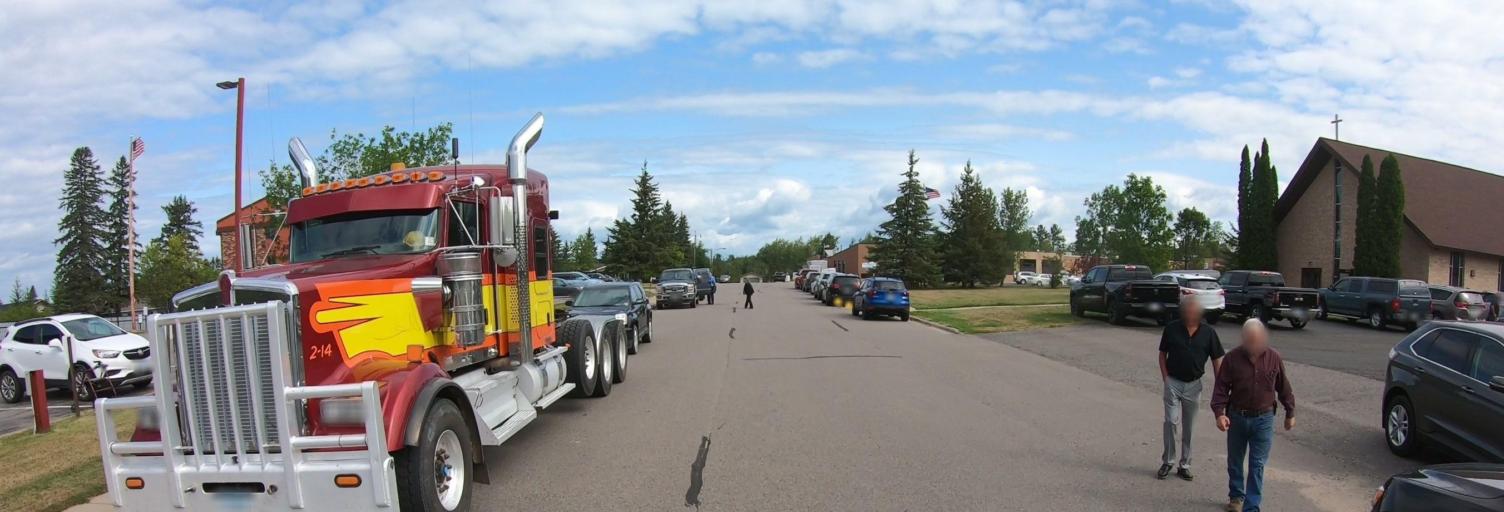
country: US
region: Minnesota
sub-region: Saint Louis County
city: Mountain Iron
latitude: 47.8517
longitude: -92.6800
